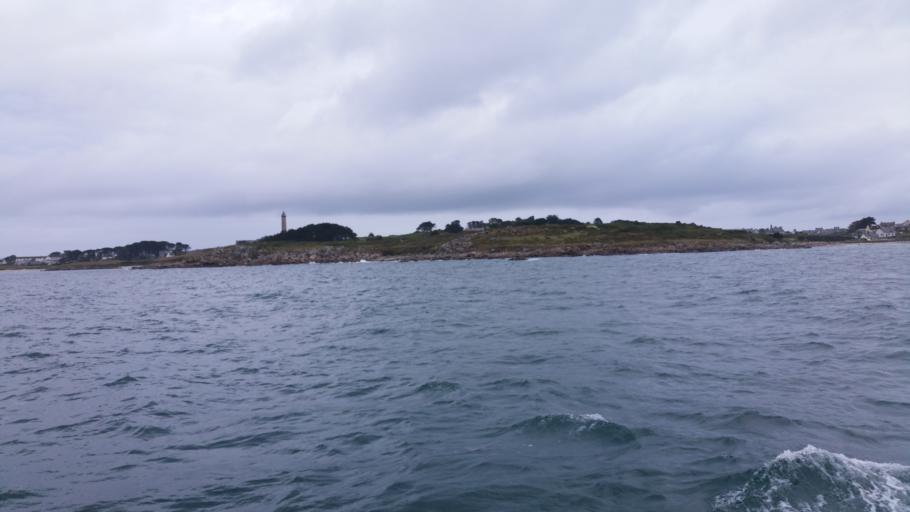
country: FR
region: Brittany
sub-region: Departement du Finistere
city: Santec
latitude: 48.7359
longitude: -4.0230
